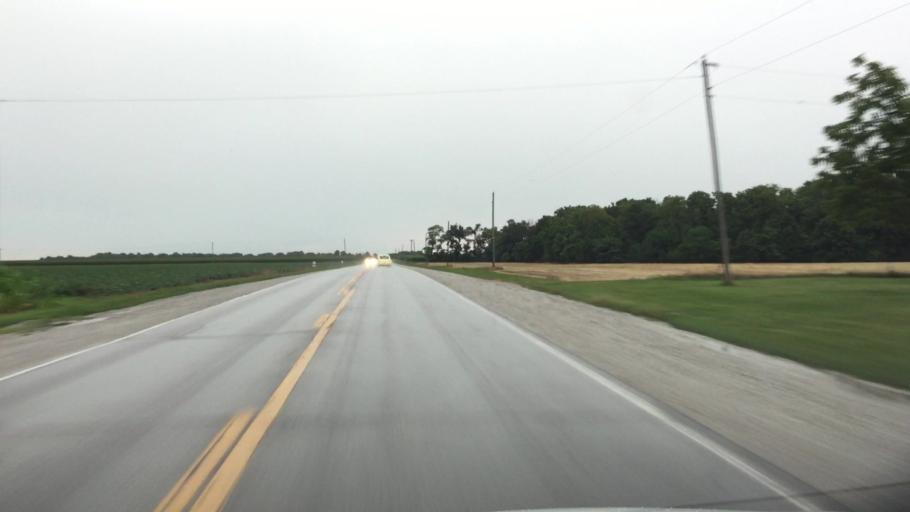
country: US
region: Illinois
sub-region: Hancock County
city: Carthage
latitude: 40.4424
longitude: -91.1399
